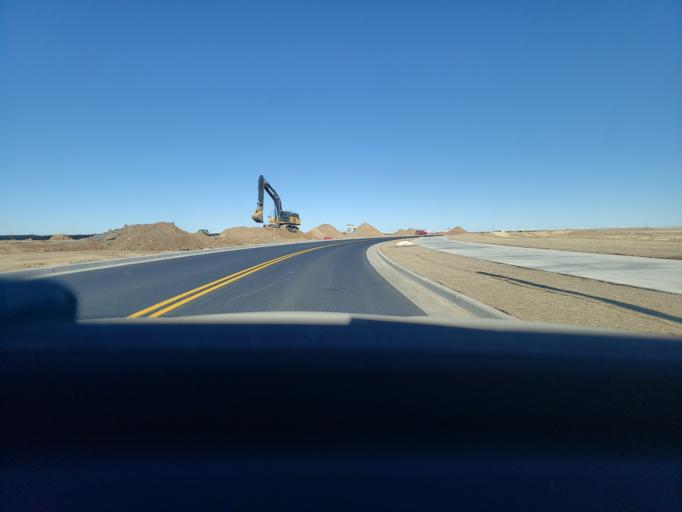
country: US
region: Colorado
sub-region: Adams County
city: Aurora
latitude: 39.7603
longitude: -104.7134
